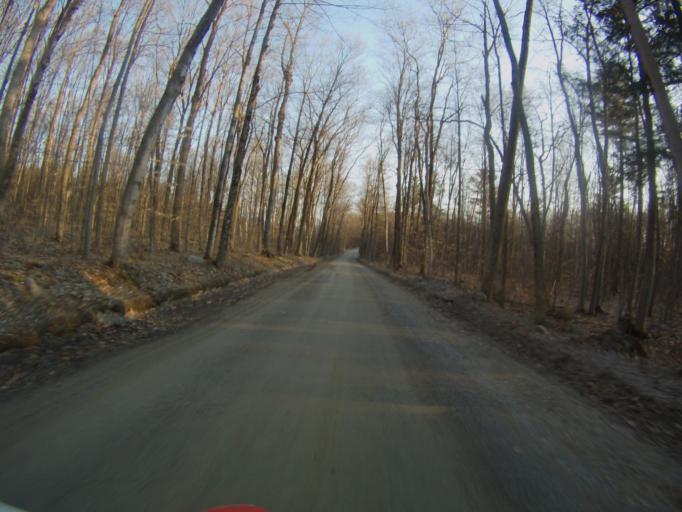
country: US
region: Vermont
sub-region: Addison County
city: Middlebury (village)
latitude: 44.0523
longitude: -73.1033
